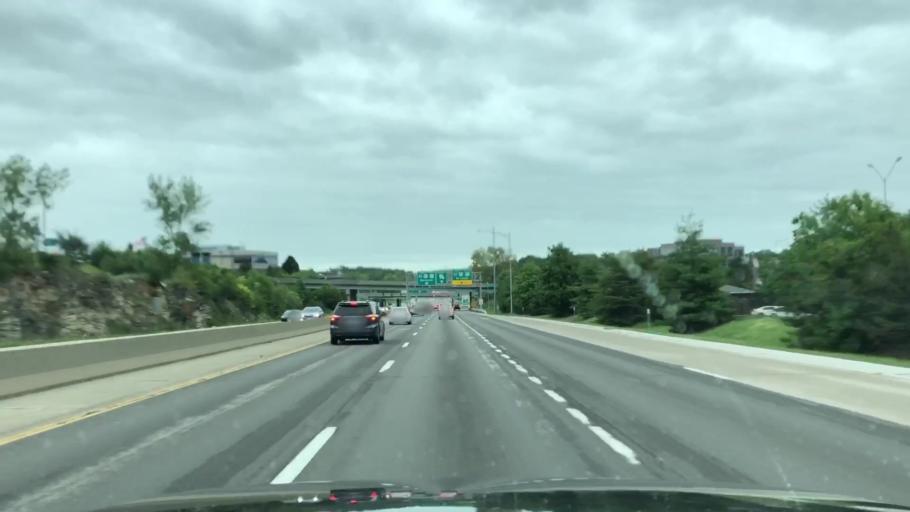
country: US
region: Missouri
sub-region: Saint Louis County
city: Manchester
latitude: 38.6383
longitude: -90.5119
